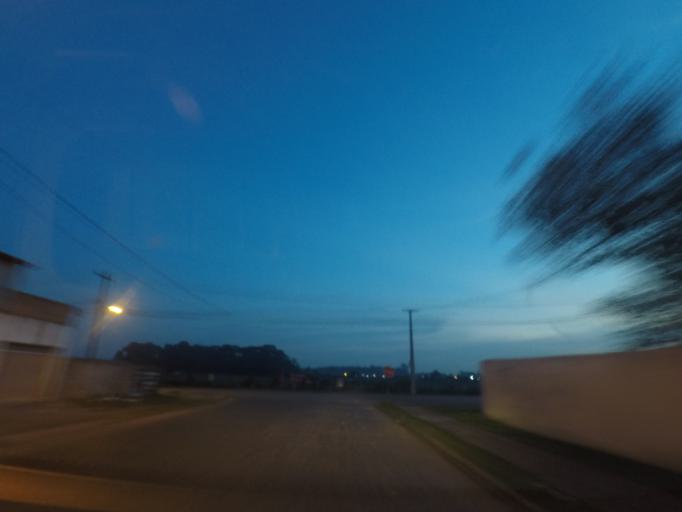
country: BR
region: Parana
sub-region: Pinhais
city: Pinhais
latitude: -25.4756
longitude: -49.1514
